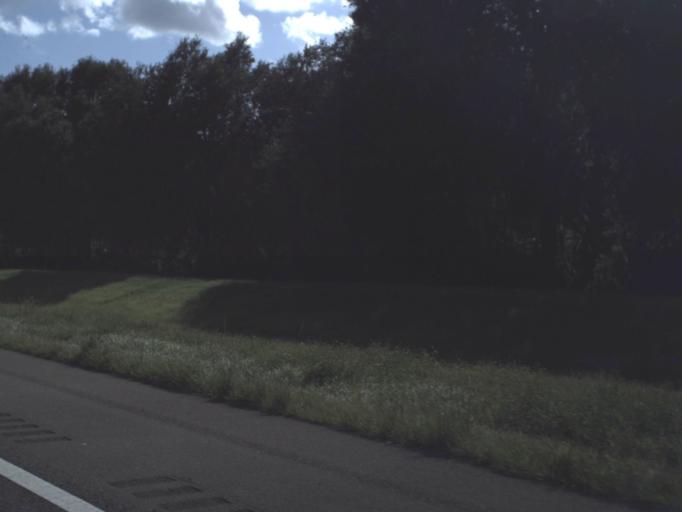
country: US
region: Florida
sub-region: Polk County
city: Fussels Corner
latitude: 28.0242
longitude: -81.8315
